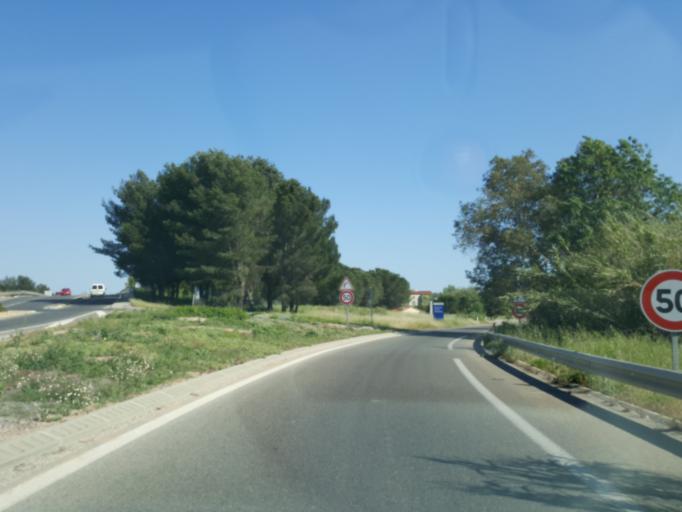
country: FR
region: Provence-Alpes-Cote d'Azur
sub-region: Departement du Var
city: Sollies-Pont
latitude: 43.1965
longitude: 6.0391
